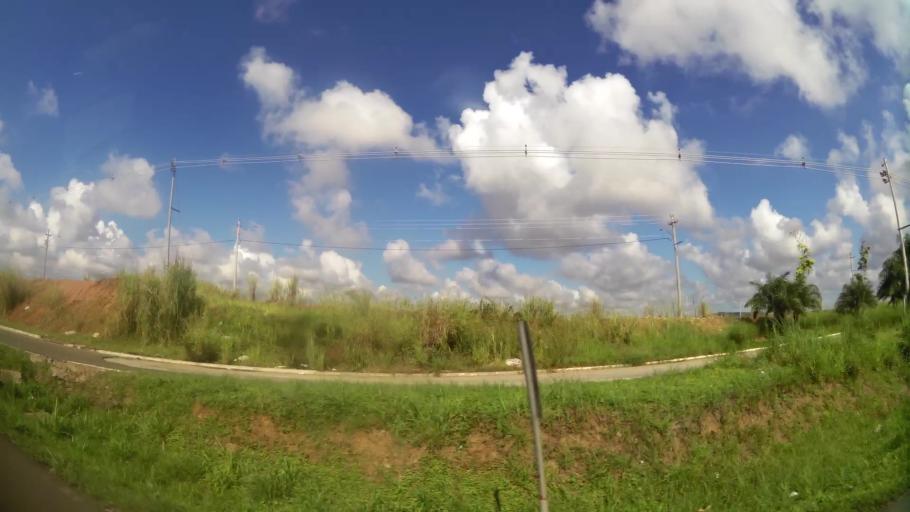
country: PA
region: Panama
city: Nuevo Arraijan
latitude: 8.8992
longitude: -79.7427
